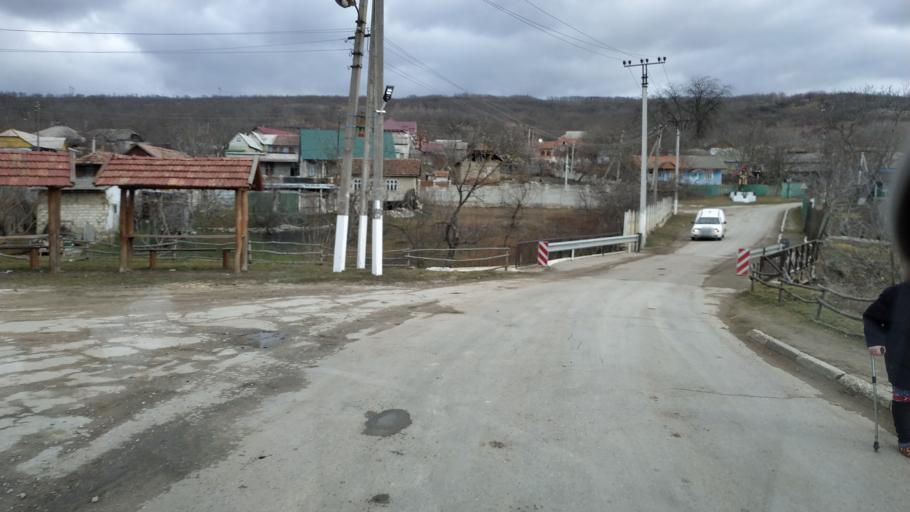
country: MD
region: Stinga Nistrului
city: Bucovat
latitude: 47.2328
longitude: 28.4436
